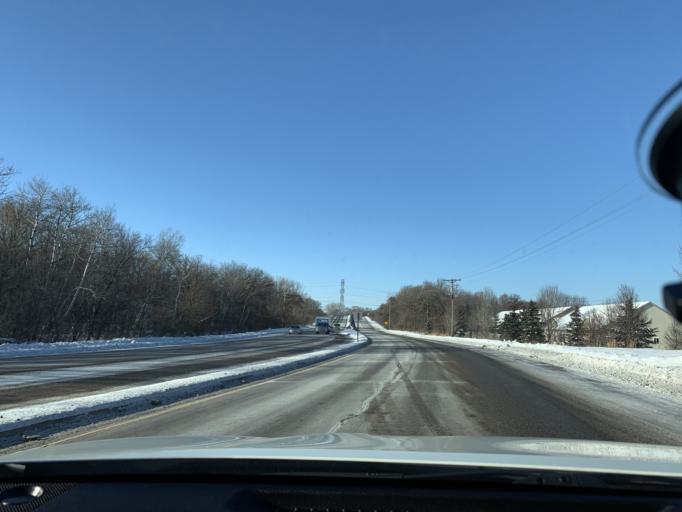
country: US
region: Minnesota
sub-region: Anoka County
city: Coon Rapids
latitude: 45.1463
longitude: -93.2847
